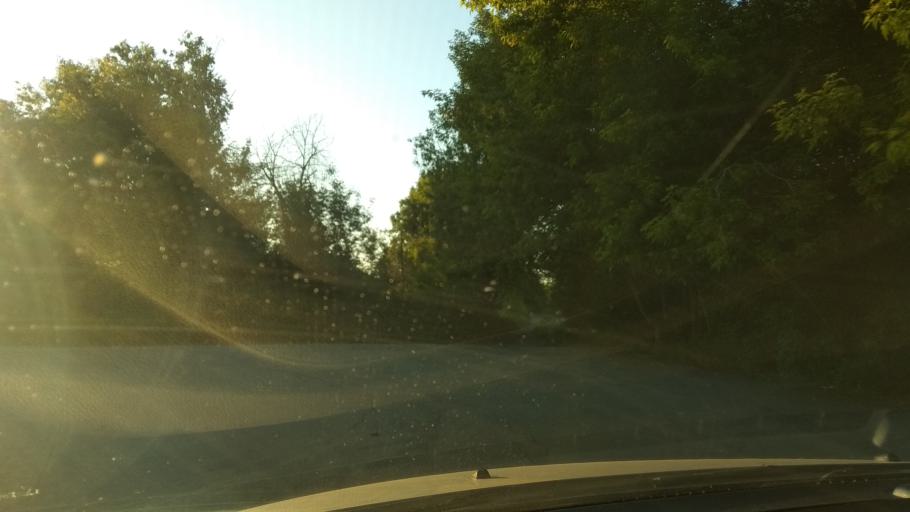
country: RU
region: Sverdlovsk
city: Sredneuralsk
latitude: 56.9825
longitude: 60.4608
